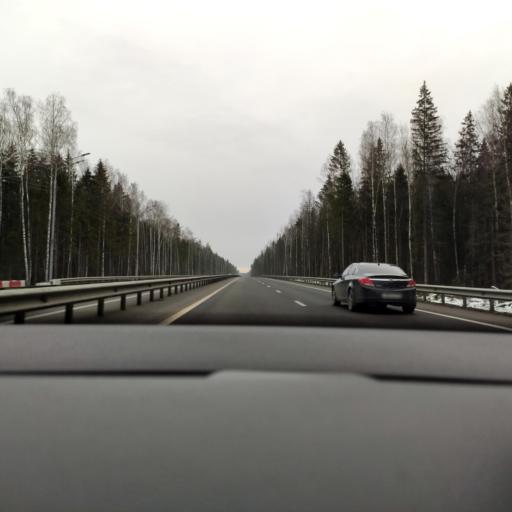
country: RU
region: Moskovskaya
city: Zvenigorod
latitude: 55.6735
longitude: 36.9094
